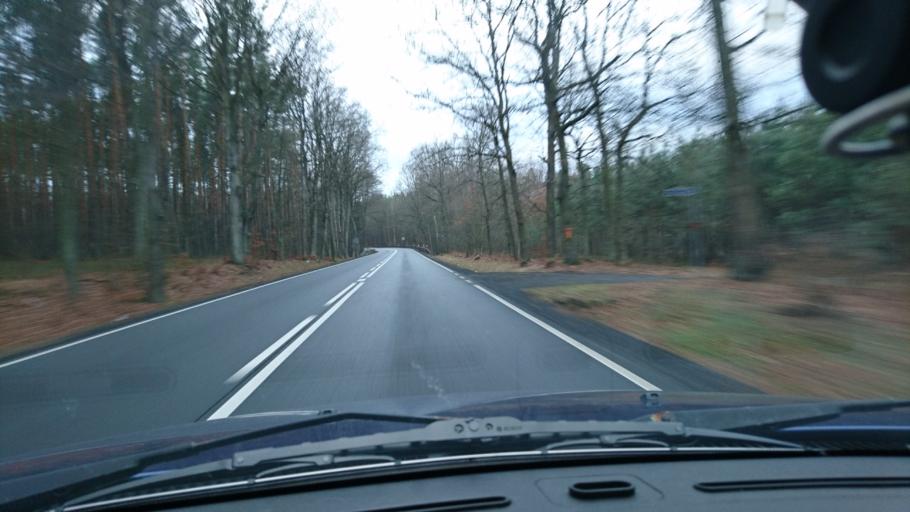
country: PL
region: Opole Voivodeship
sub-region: Powiat oleski
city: Olesno
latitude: 50.9354
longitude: 18.3310
